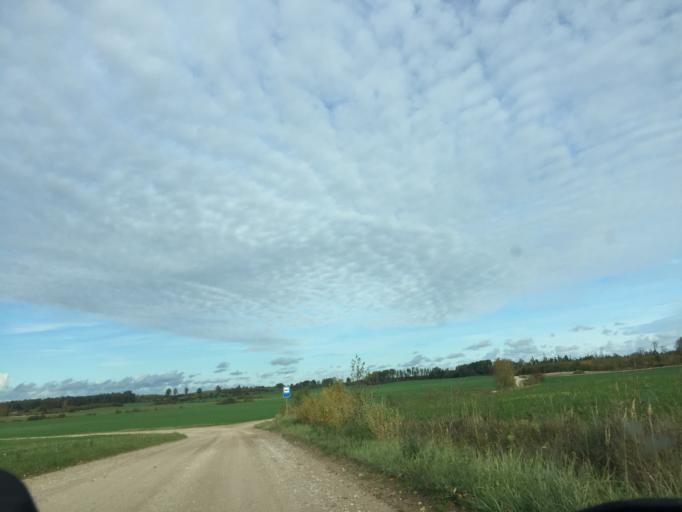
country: LV
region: Jaunpils
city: Jaunpils
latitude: 56.6273
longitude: 23.0618
